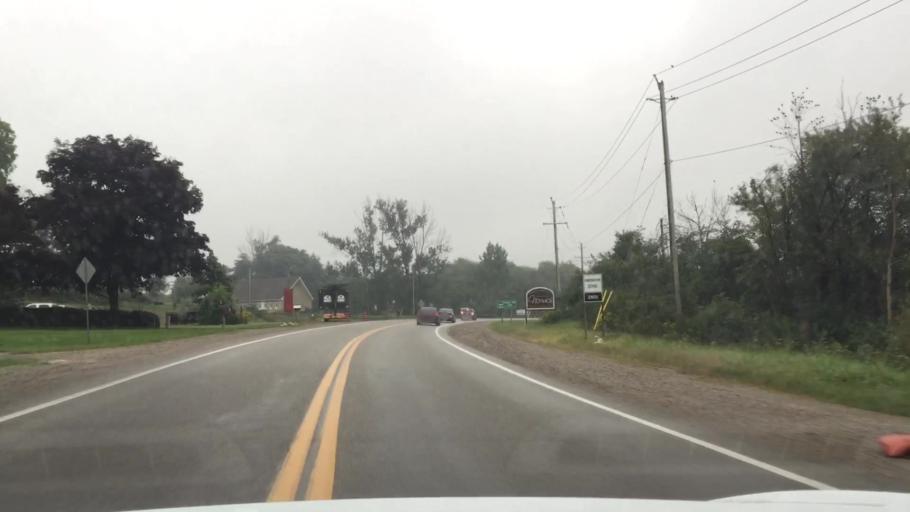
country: CA
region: Ontario
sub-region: Oxford County
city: Woodstock
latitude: 43.1065
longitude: -80.7325
